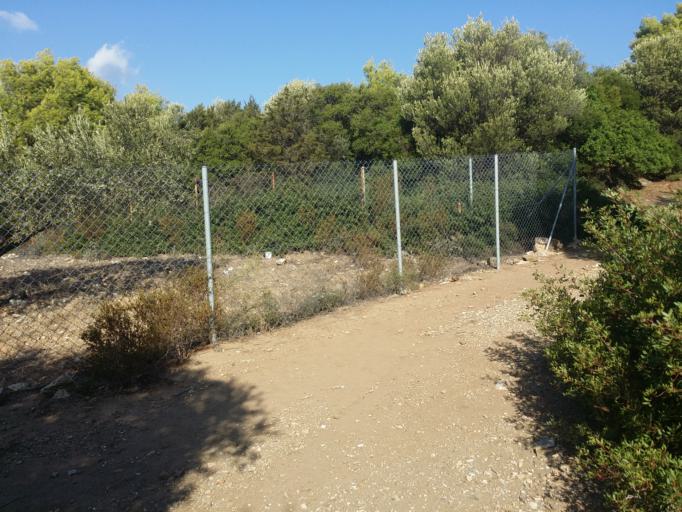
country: GR
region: Attica
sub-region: Nomarchia Anatolikis Attikis
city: Kato Soulion
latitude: 38.2155
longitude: 24.0267
